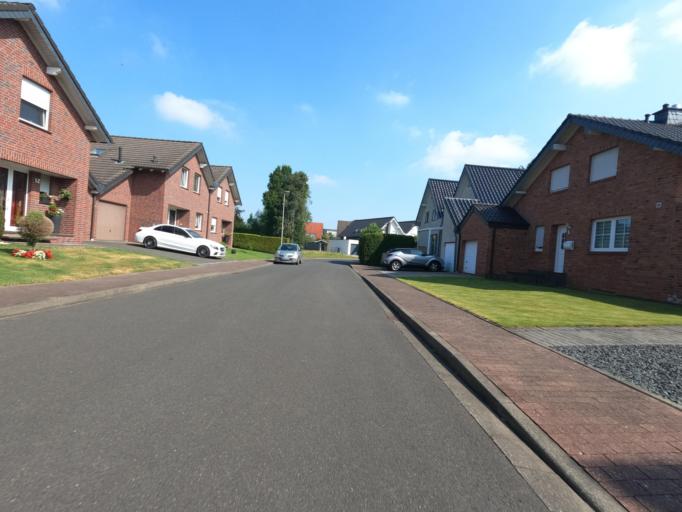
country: DE
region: North Rhine-Westphalia
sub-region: Regierungsbezirk Koln
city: Heinsberg
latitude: 51.0705
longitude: 6.1001
